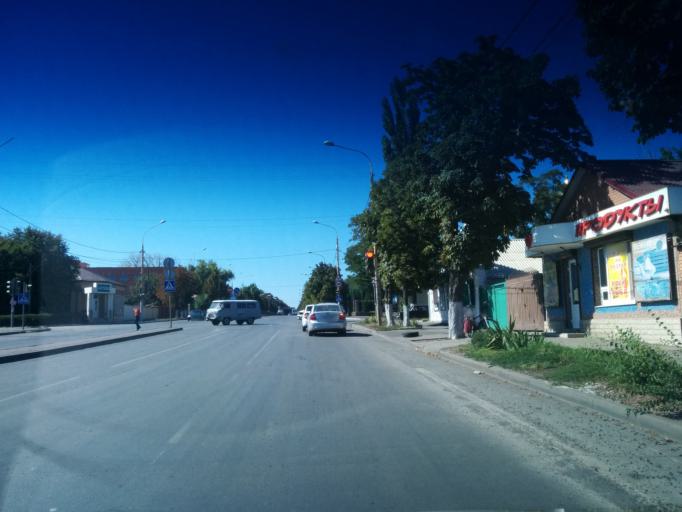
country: RU
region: Rostov
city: Shakhty
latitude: 47.7029
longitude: 40.2280
